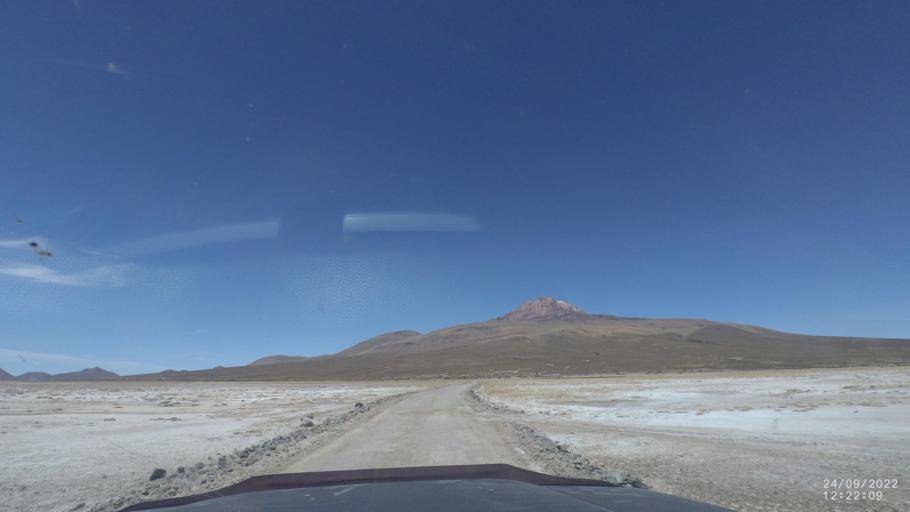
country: BO
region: Potosi
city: Colchani
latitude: -19.7541
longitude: -67.6662
